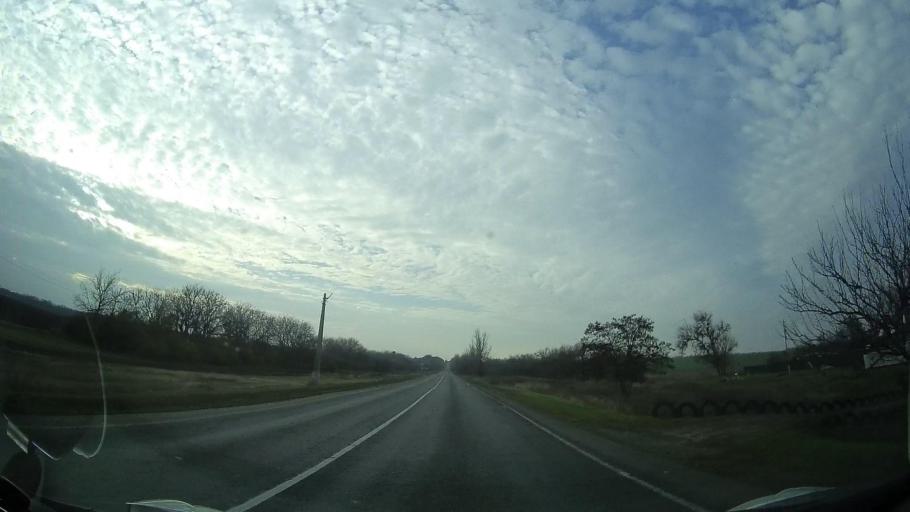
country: RU
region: Rostov
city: Bagayevskaya
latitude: 47.0960
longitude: 40.3107
